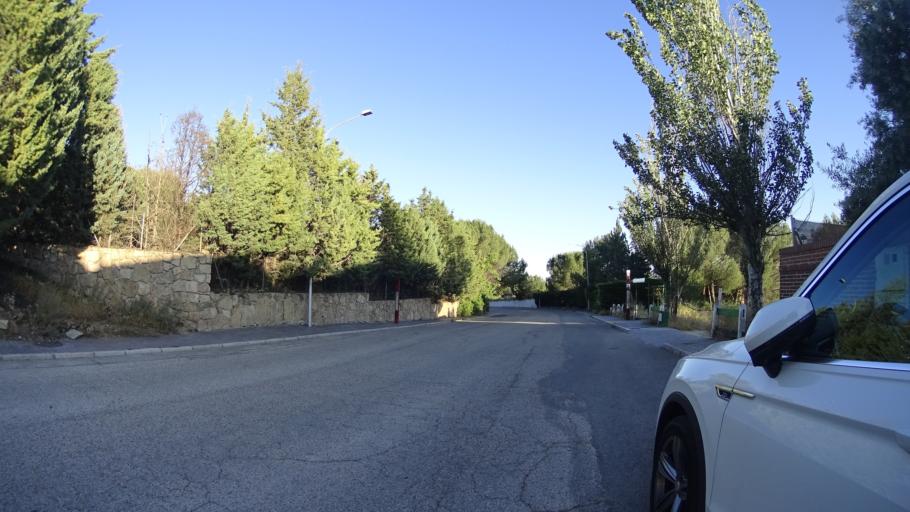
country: ES
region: Madrid
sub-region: Provincia de Madrid
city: Galapagar
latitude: 40.5929
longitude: -3.9682
